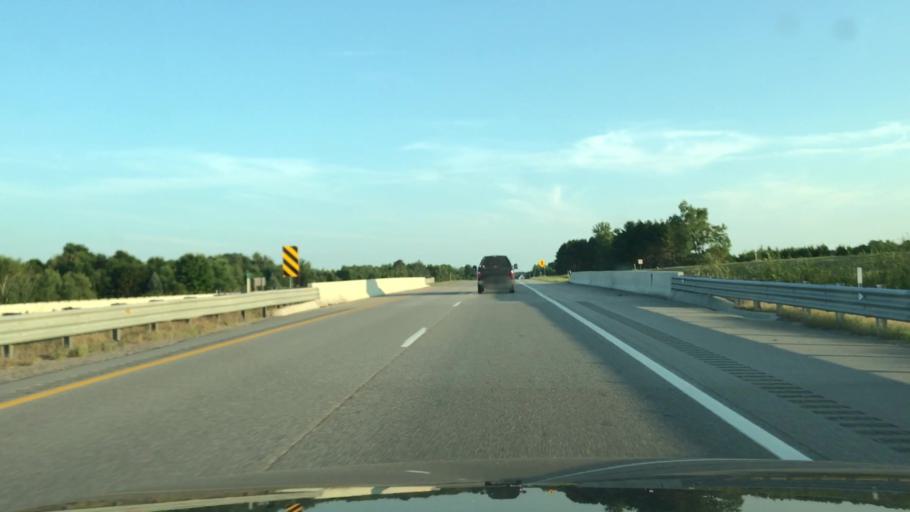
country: US
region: Michigan
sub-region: Osceola County
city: Reed City
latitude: 43.8846
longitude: -85.5282
